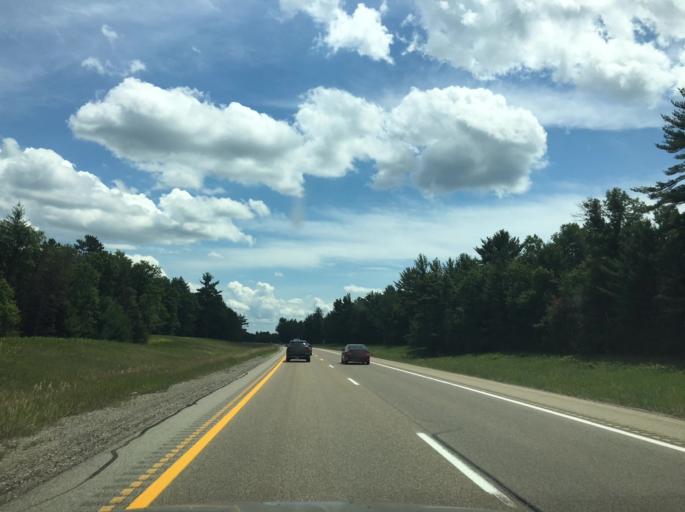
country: US
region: Michigan
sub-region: Crawford County
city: Grayling
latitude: 44.5488
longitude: -84.7026
